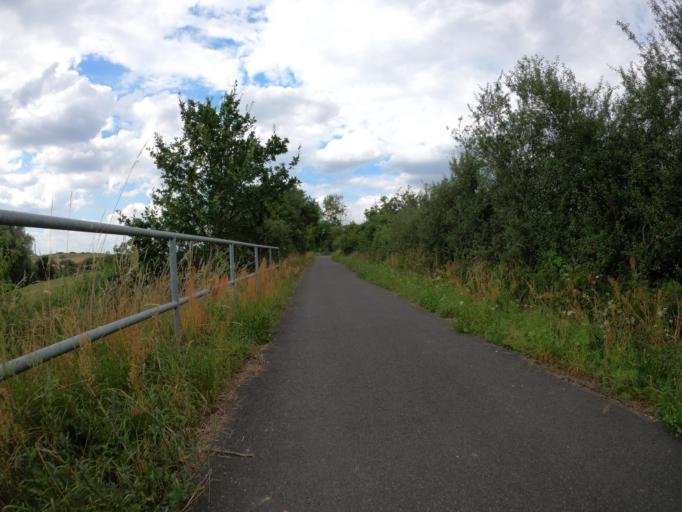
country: DE
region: Mecklenburg-Vorpommern
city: Woldegk
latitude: 53.3697
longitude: 13.5891
